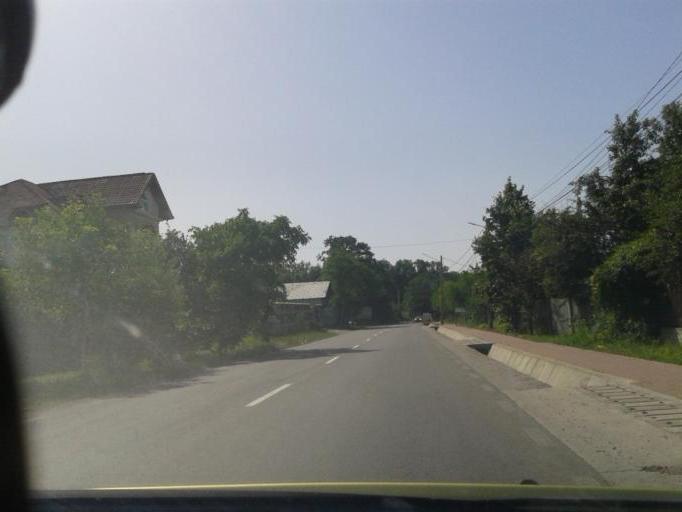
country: RO
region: Prahova
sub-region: Comuna Paulesti
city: Gageni
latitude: 45.0158
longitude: 25.9495
